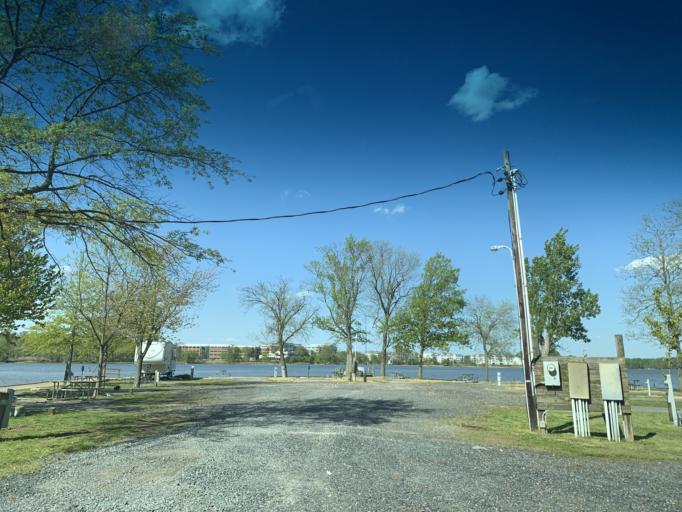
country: US
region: Maryland
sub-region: Harford County
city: Riverside
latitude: 39.4611
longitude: -76.2420
